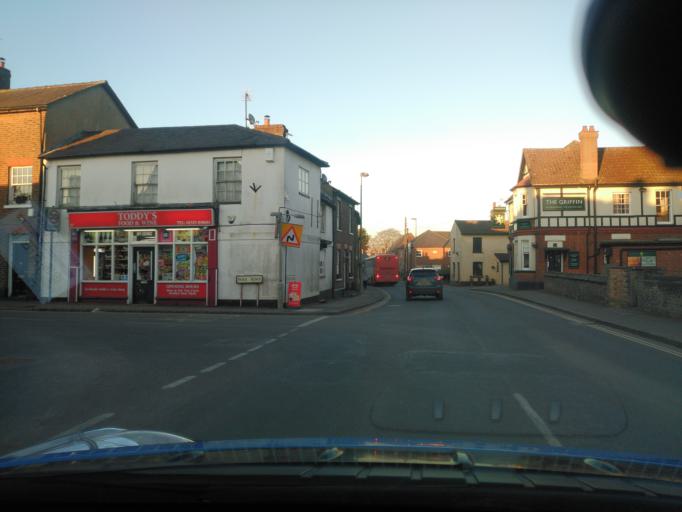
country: GB
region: England
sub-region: Central Bedfordshire
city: Toddington
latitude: 51.9501
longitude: -0.5320
